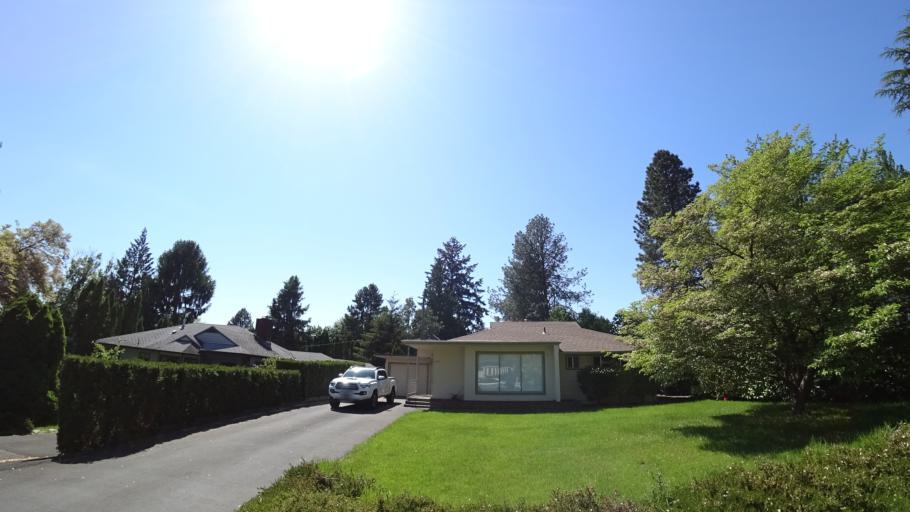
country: US
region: Oregon
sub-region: Washington County
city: Cedar Hills
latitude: 45.4990
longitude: -122.8014
